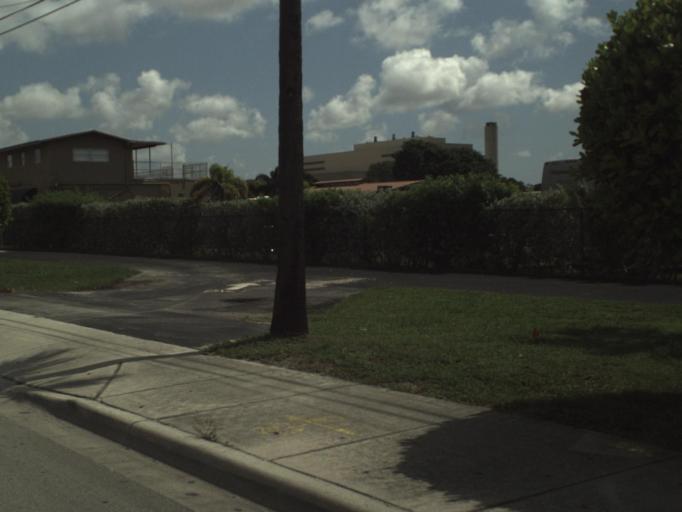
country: US
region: Florida
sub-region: Broward County
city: Davie
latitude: 26.0650
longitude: -80.2078
